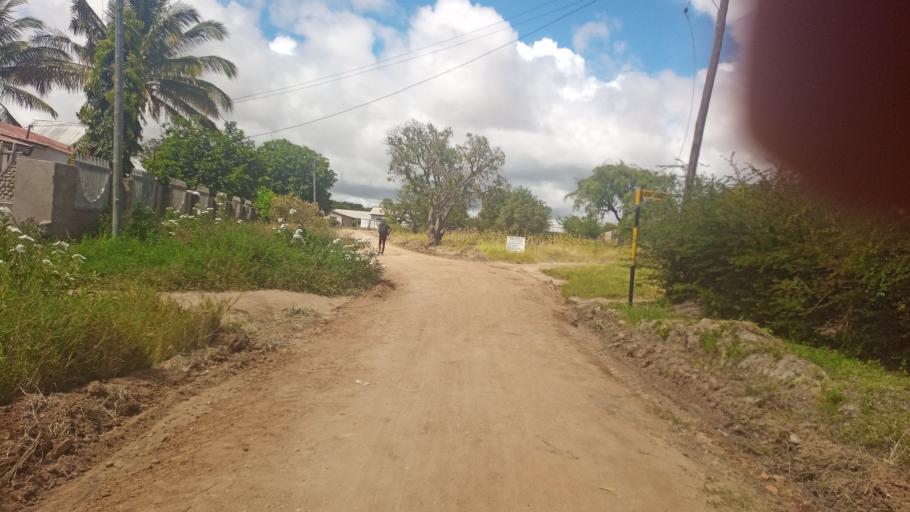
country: TZ
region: Dodoma
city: Dodoma
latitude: -6.1928
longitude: 35.7288
